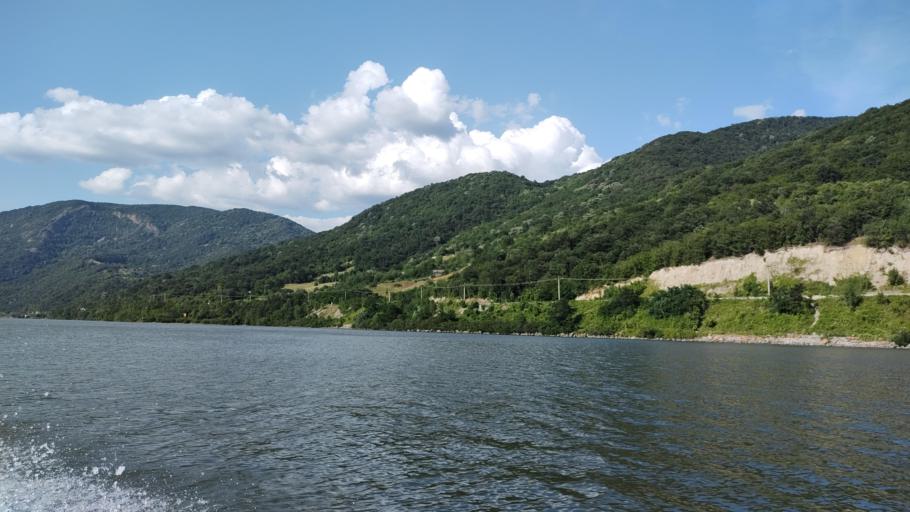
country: RO
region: Mehedinti
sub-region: Comuna Svinita
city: Svinita
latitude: 44.5680
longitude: 22.0293
